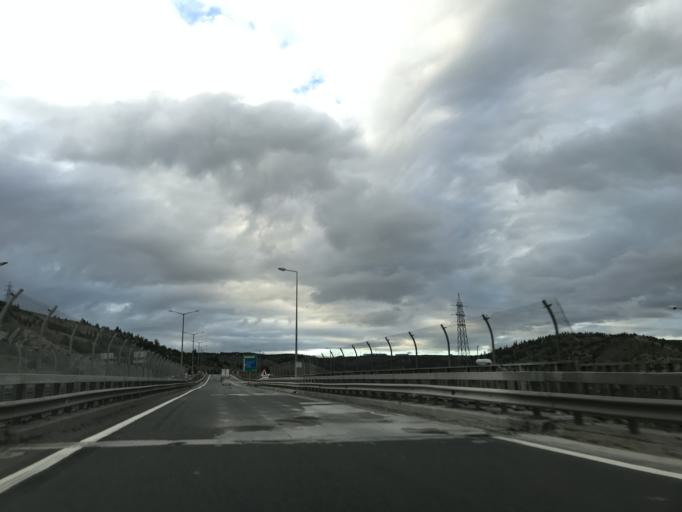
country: TR
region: Ankara
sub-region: Goelbasi
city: Golbasi
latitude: 39.8094
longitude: 32.8007
